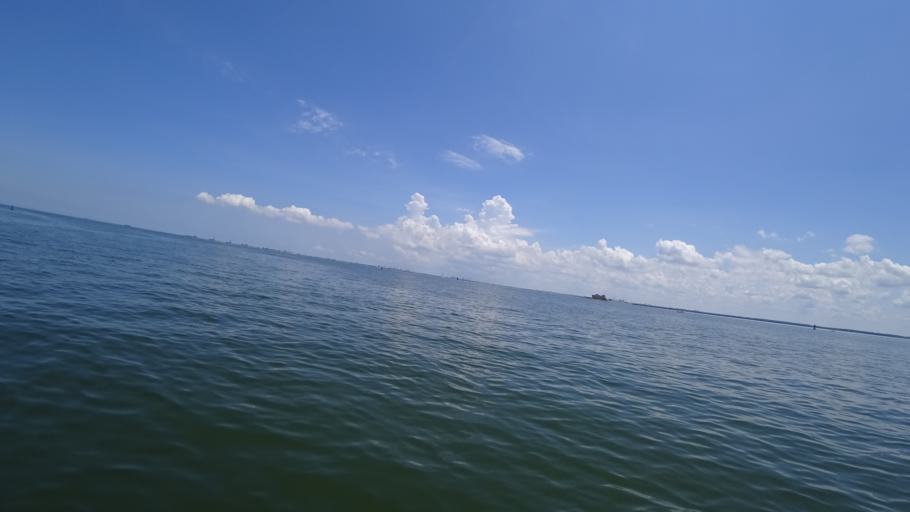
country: US
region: Virginia
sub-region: City of Newport News
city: Newport News
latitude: 36.9566
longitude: -76.4127
